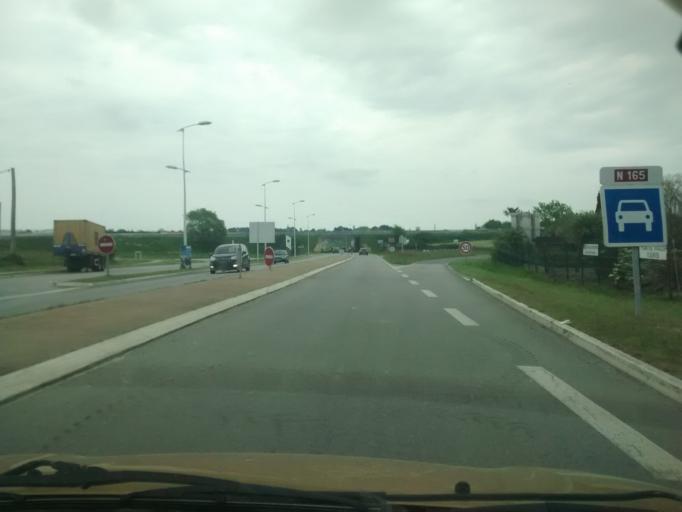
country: FR
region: Brittany
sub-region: Departement du Morbihan
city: Muzillac
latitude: 47.5591
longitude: -2.5041
